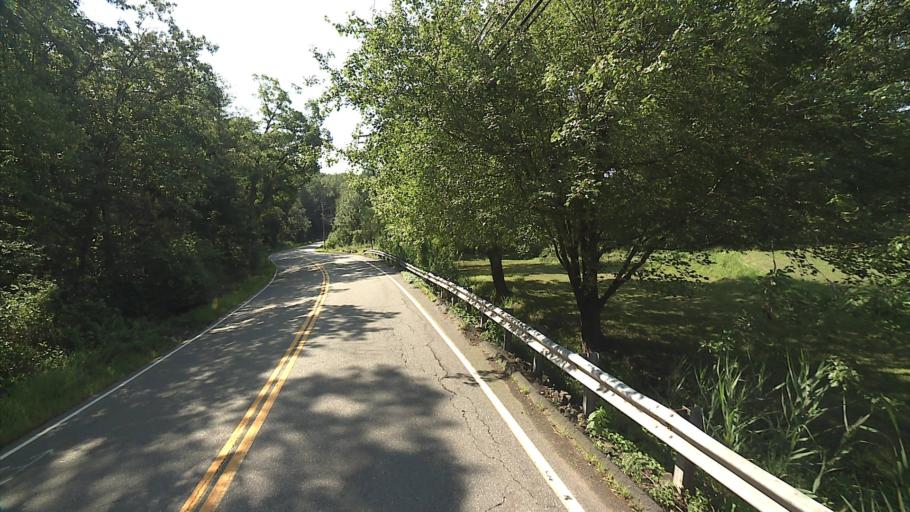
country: US
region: Connecticut
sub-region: New Haven County
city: North Branford
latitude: 41.2785
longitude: -72.7596
